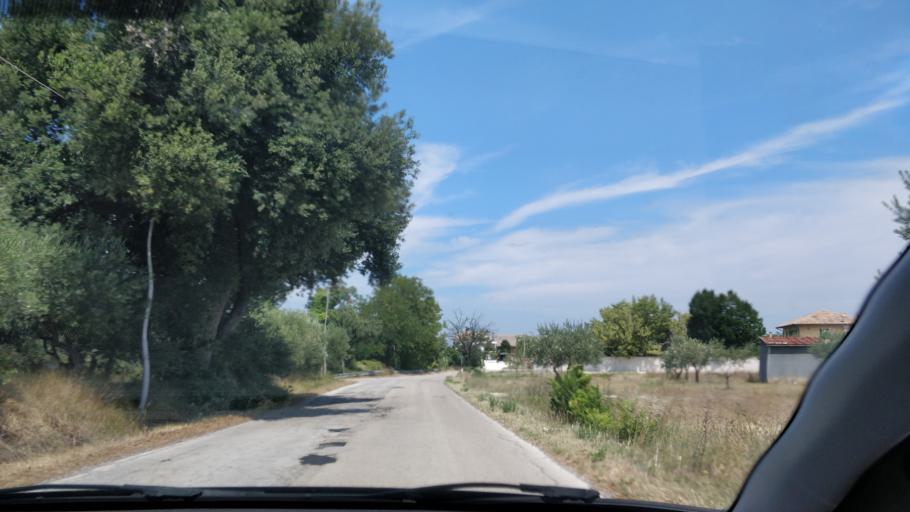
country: IT
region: Abruzzo
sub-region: Provincia di Chieti
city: Torrevecchia
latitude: 42.3955
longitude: 14.2002
